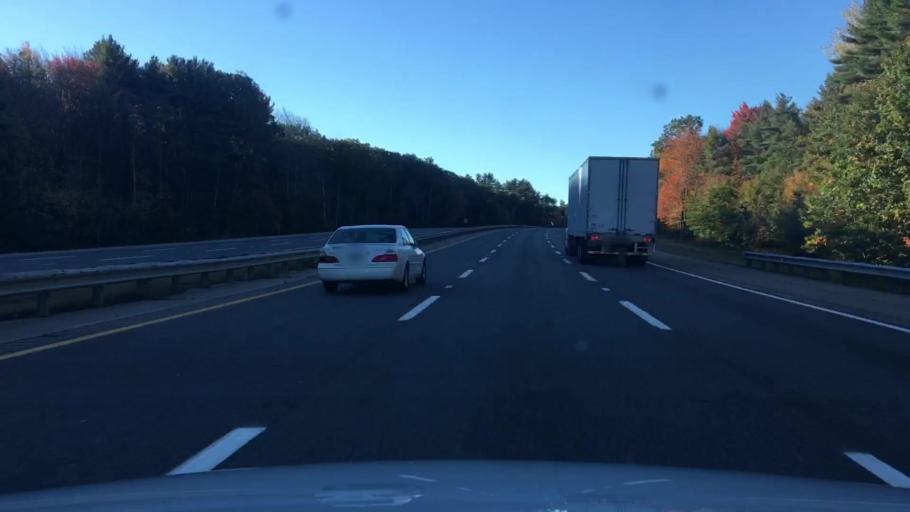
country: US
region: Maine
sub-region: York County
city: Ogunquit
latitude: 43.2598
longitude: -70.6198
